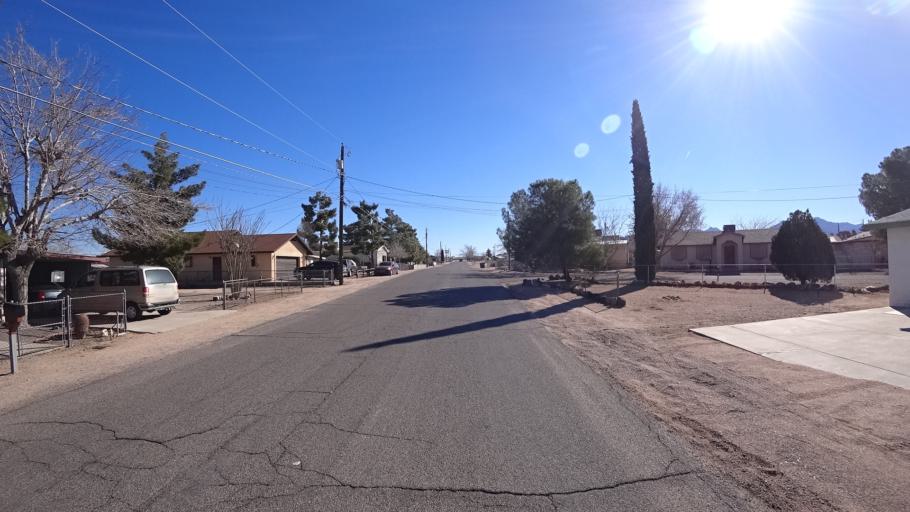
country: US
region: Arizona
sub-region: Mohave County
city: Kingman
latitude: 35.2031
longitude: -114.0287
